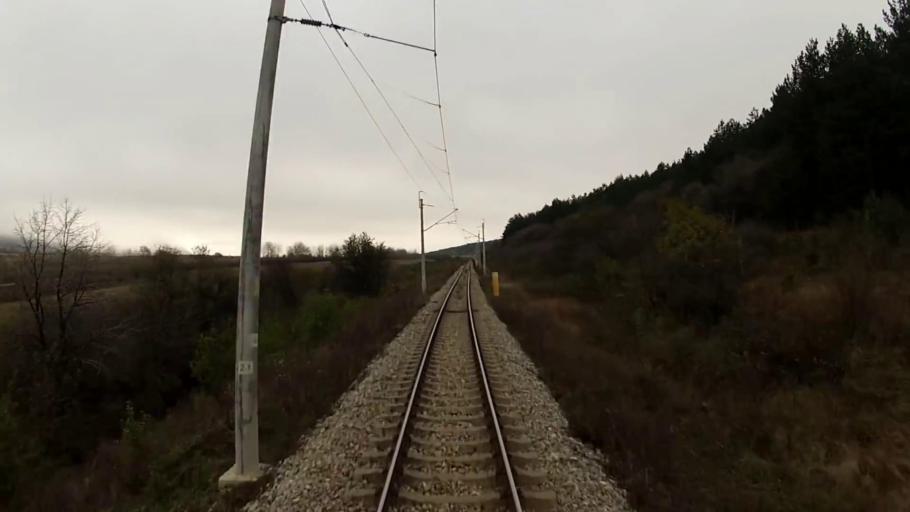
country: BG
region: Sofiya
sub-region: Obshtina Dragoman
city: Dragoman
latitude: 42.9324
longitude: 22.9087
